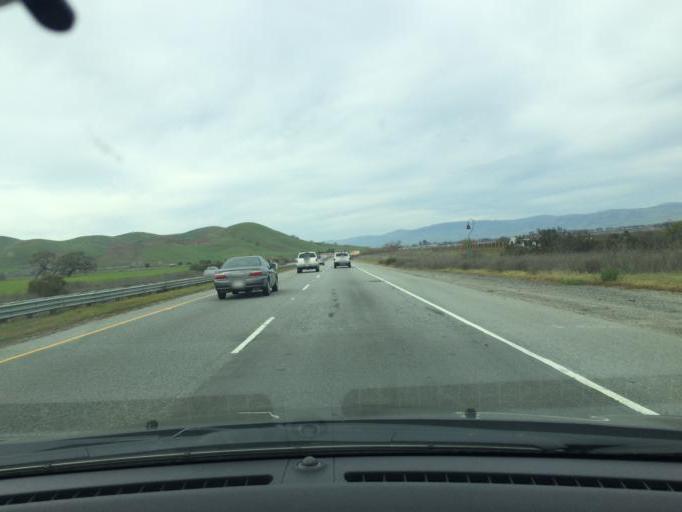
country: US
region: California
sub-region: Santa Clara County
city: Gilroy
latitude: 36.9387
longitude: -121.5525
